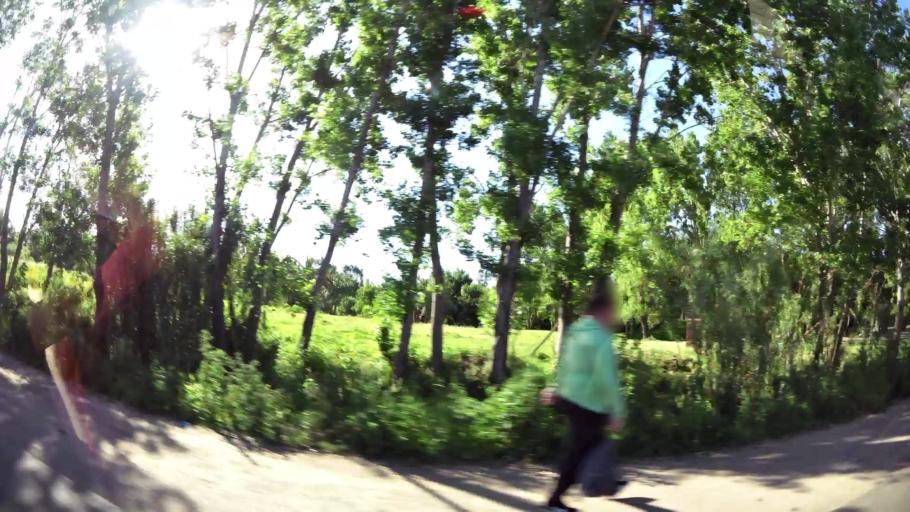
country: UY
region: Montevideo
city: Montevideo
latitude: -34.8267
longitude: -56.1826
